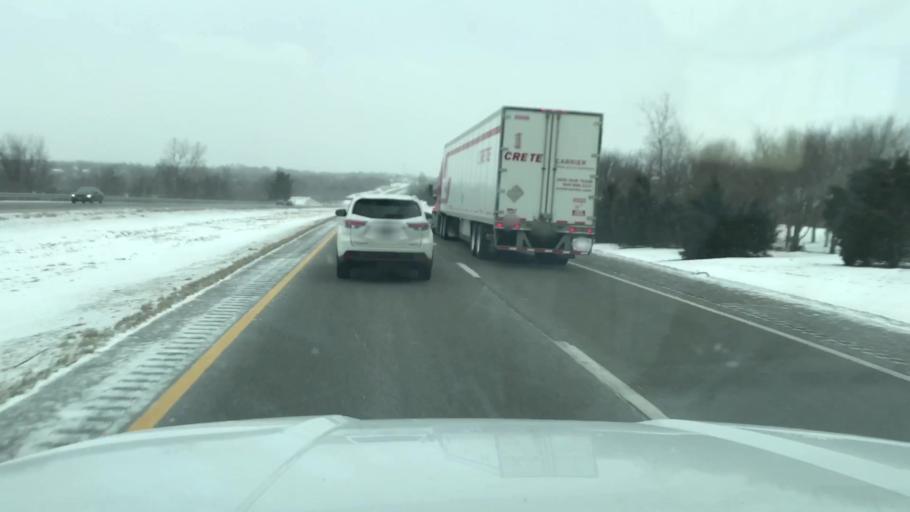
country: US
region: Missouri
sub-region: Andrew County
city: Country Club Village
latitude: 39.7977
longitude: -94.7982
